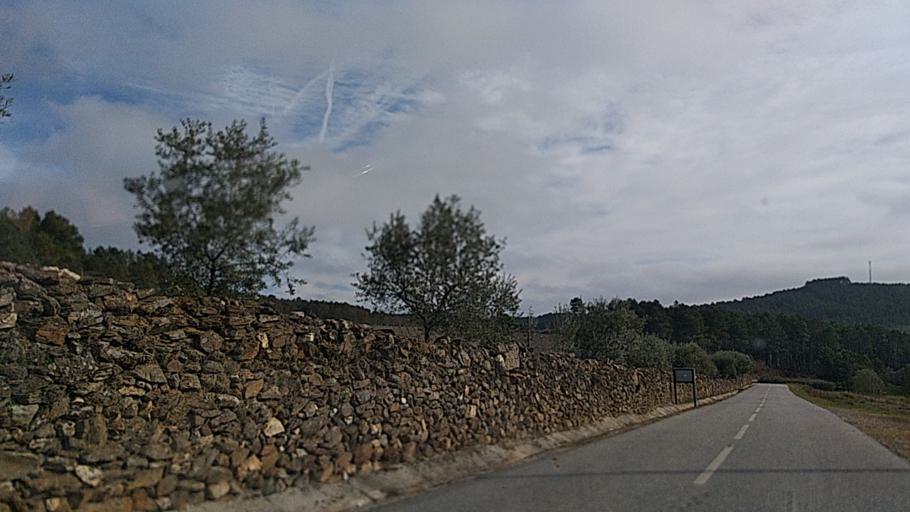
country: PT
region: Guarda
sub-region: Fornos de Algodres
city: Fornos de Algodres
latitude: 40.6886
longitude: -7.5487
